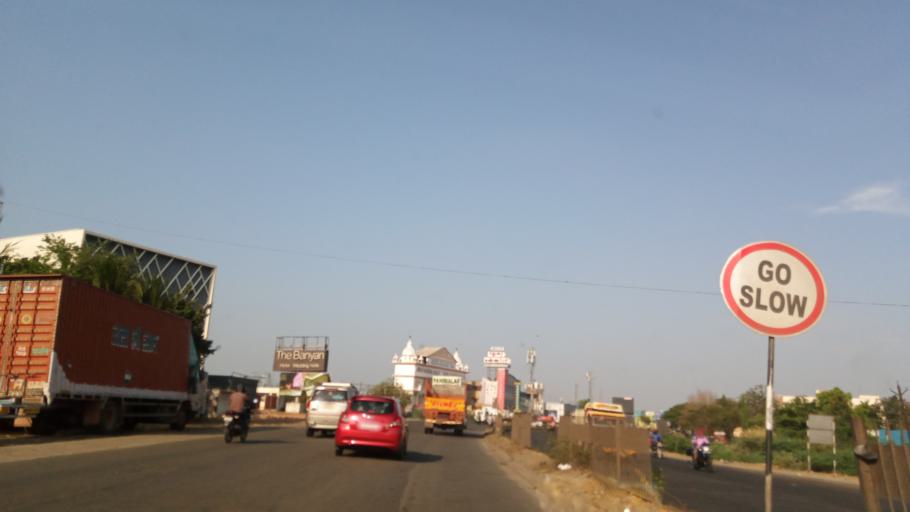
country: IN
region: Tamil Nadu
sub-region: Kancheepuram
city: Poonamalle
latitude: 13.0466
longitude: 80.0741
